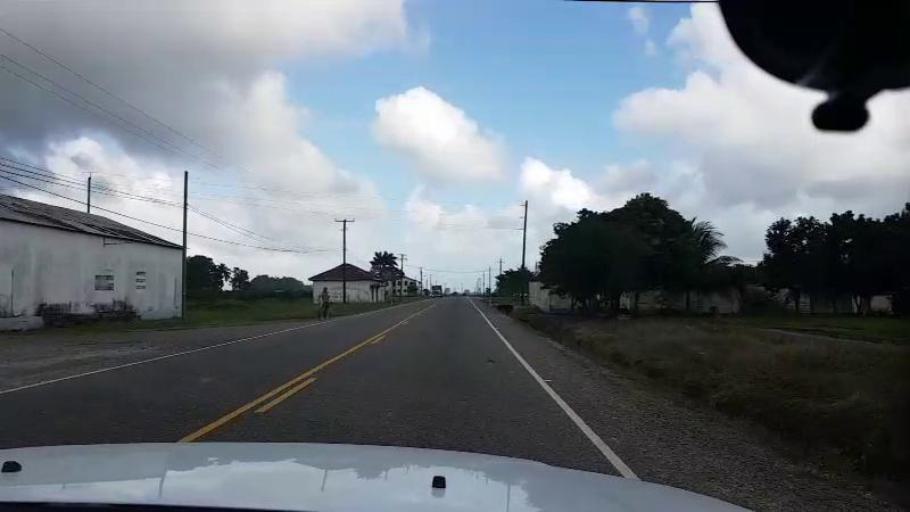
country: BZ
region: Stann Creek
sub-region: Dangriga
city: Dangriga
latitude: 16.9947
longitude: -88.3700
